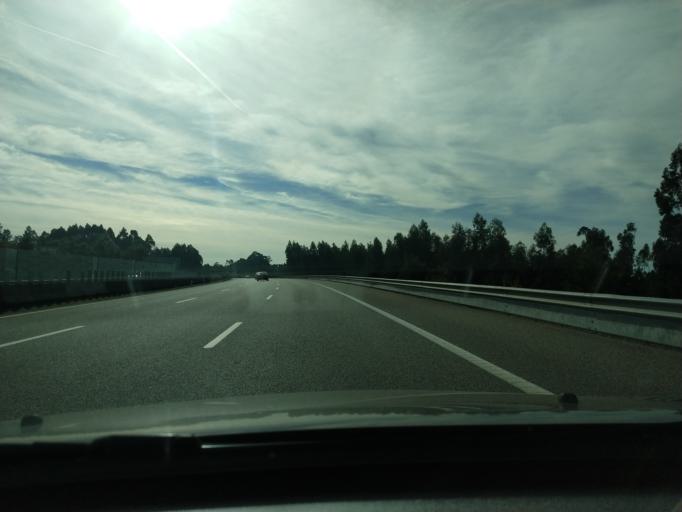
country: PT
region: Aveiro
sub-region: Santa Maria da Feira
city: Pacos de Brandao
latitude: 40.9699
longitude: -8.5714
